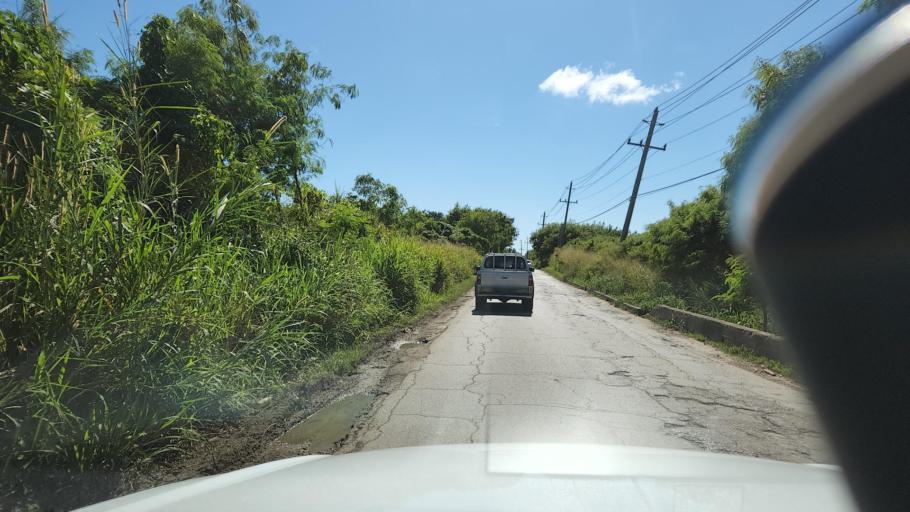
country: BB
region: Saint Thomas
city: Welchman Hall
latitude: 13.1786
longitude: -59.5981
